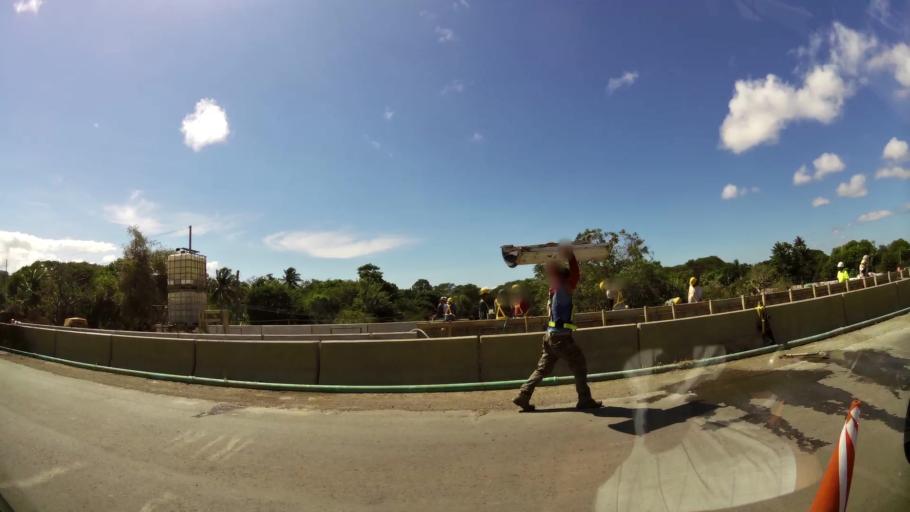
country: CR
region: Guanacaste
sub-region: Canton de Canas
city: Canas
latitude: 10.4211
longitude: -85.0889
